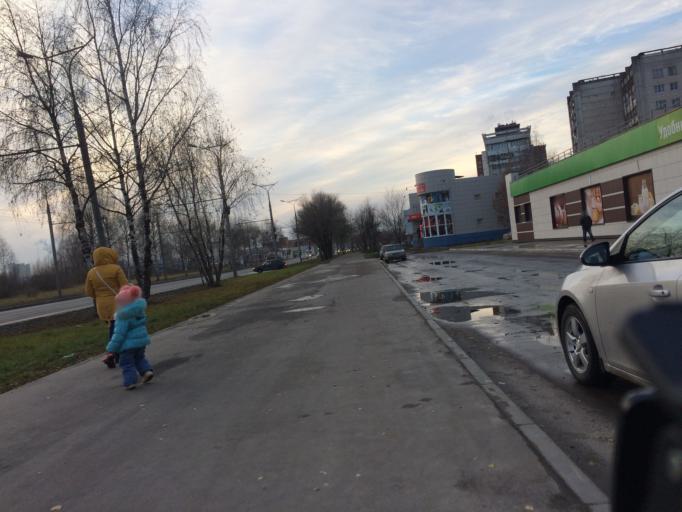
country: RU
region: Mariy-El
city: Yoshkar-Ola
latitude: 56.6268
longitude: 47.9121
